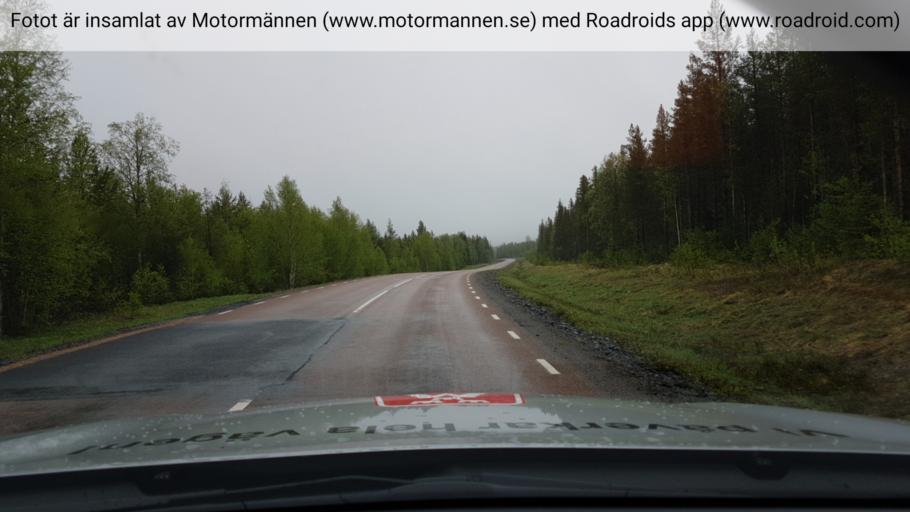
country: SE
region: Jaemtland
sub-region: Krokoms Kommun
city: Valla
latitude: 63.1785
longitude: 14.0062
